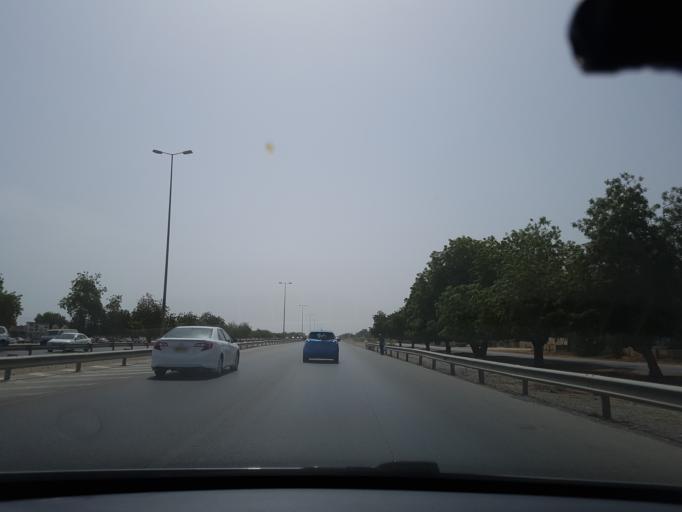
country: OM
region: Al Batinah
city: As Suwayq
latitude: 23.8375
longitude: 57.3828
